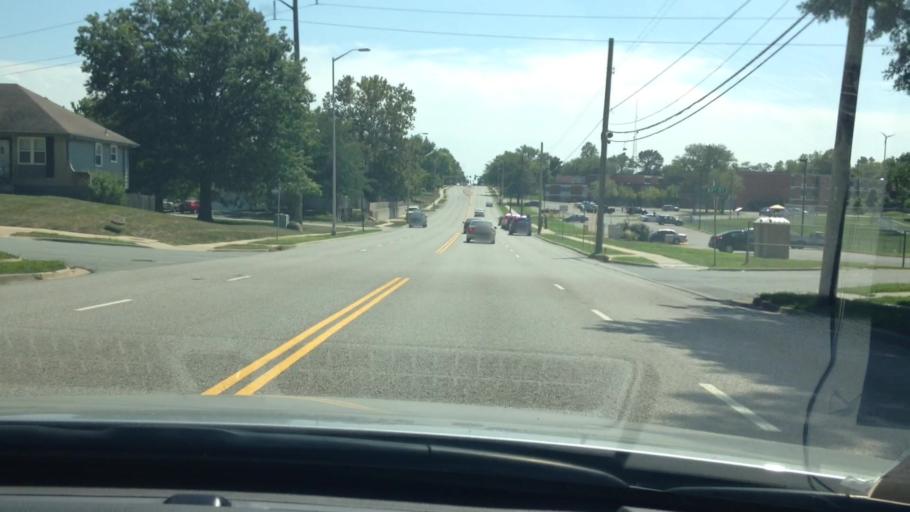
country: US
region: Kansas
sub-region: Johnson County
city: Overland Park
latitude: 38.9788
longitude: -94.6864
